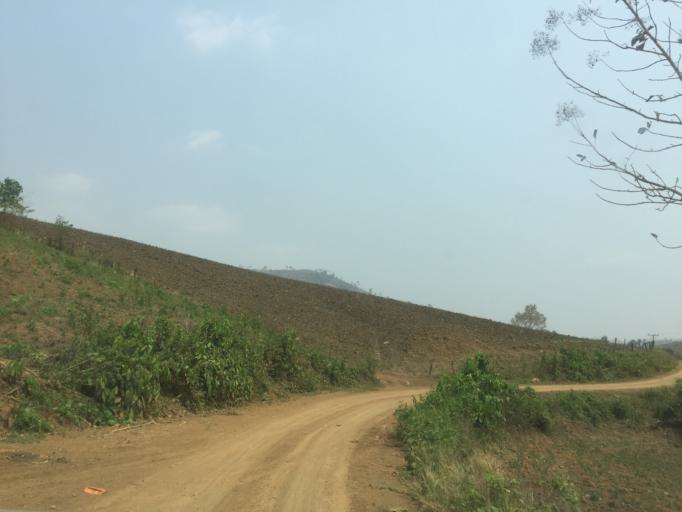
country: LA
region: Xiagnabouli
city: Muang Kenthao
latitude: 17.8089
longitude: 101.2697
